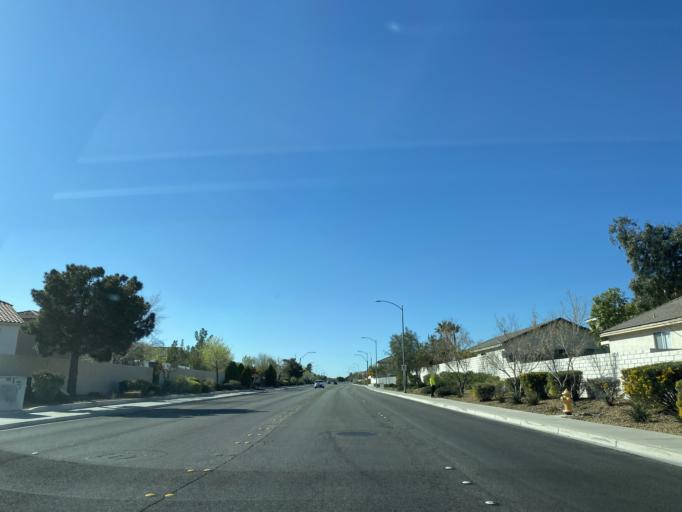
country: US
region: Nevada
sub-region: Clark County
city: Summerlin South
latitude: 36.3122
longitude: -115.2877
